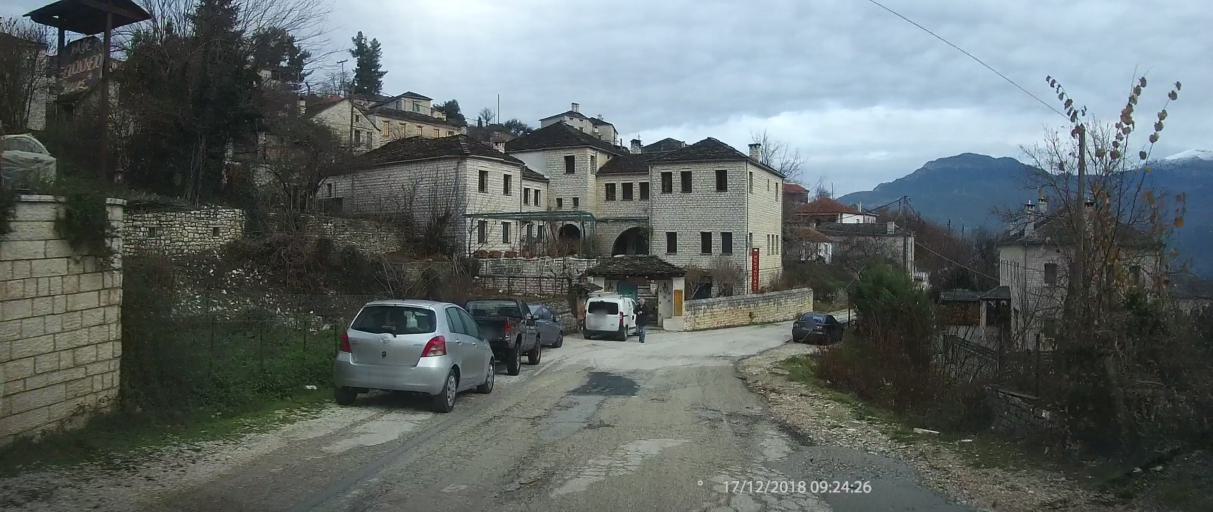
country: GR
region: Epirus
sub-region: Nomos Ioanninon
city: Kalpaki
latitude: 39.9346
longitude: 20.6722
